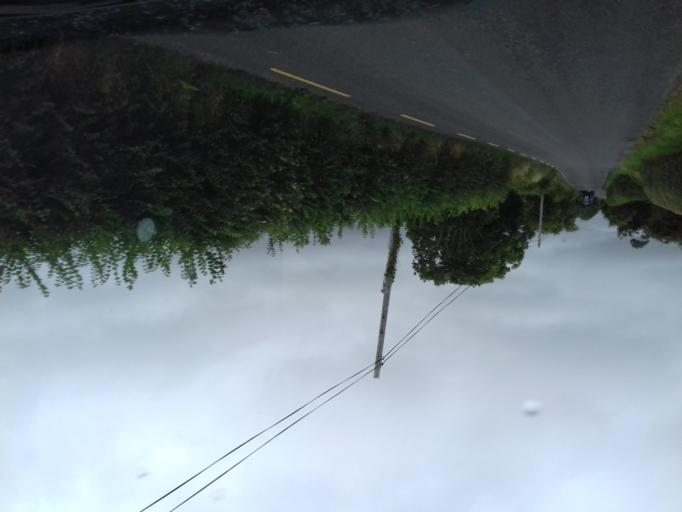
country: IE
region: Leinster
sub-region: Kilkenny
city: Graiguenamanagh
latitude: 52.6160
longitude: -7.0352
